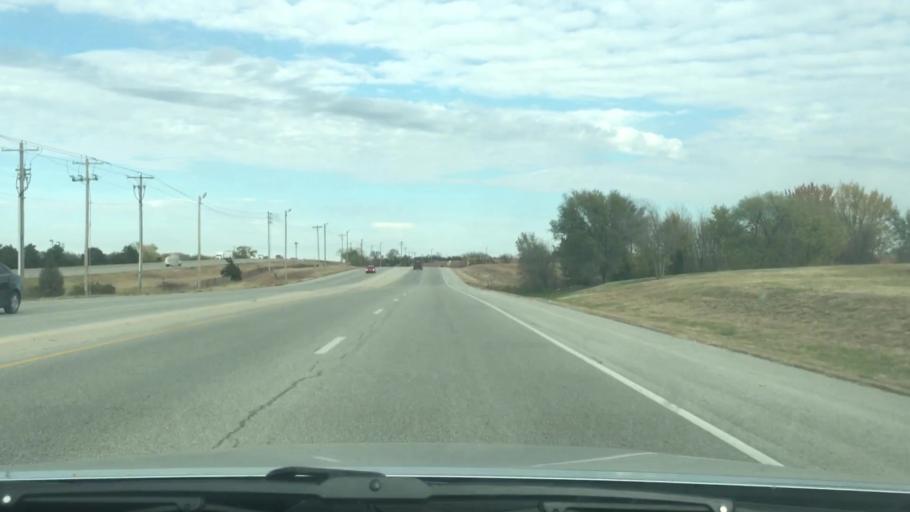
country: US
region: Kansas
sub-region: Sedgwick County
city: Wichita
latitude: 37.6524
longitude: -97.2665
